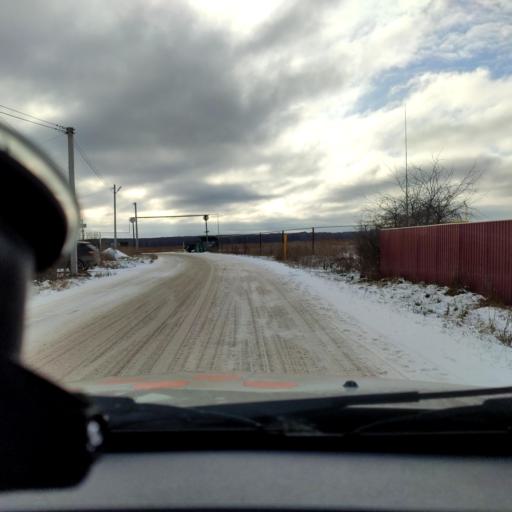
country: RU
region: Bashkortostan
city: Avdon
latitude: 54.7847
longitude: 55.7278
